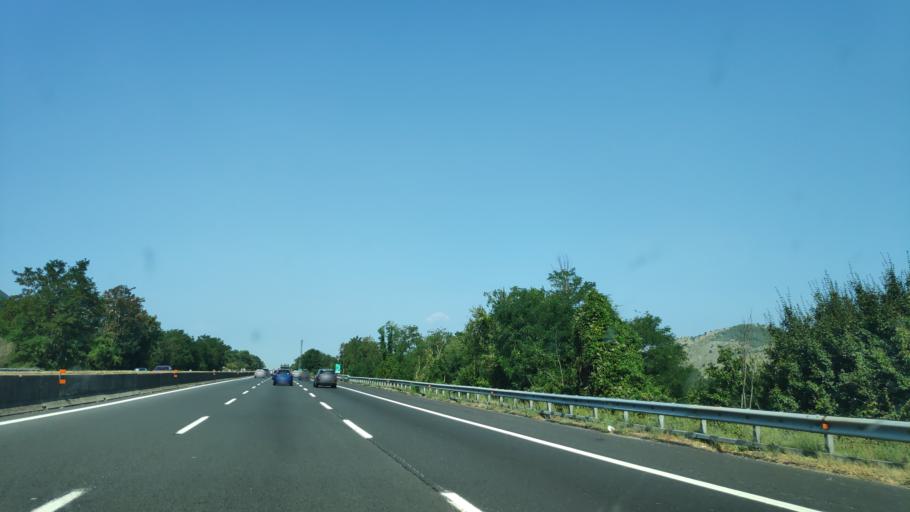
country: IT
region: Campania
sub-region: Provincia di Caserta
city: Mignano Monte Lungo
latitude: 41.4056
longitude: 13.9678
